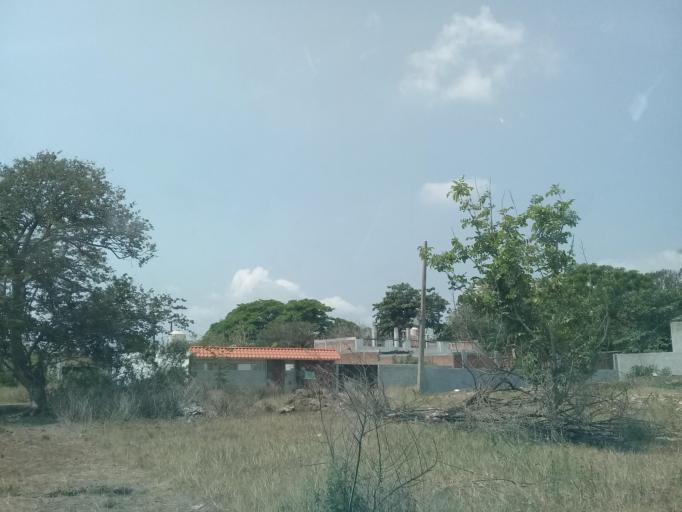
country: MX
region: Veracruz
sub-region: Veracruz
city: Hacienda Sotavento
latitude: 19.1354
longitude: -96.1788
